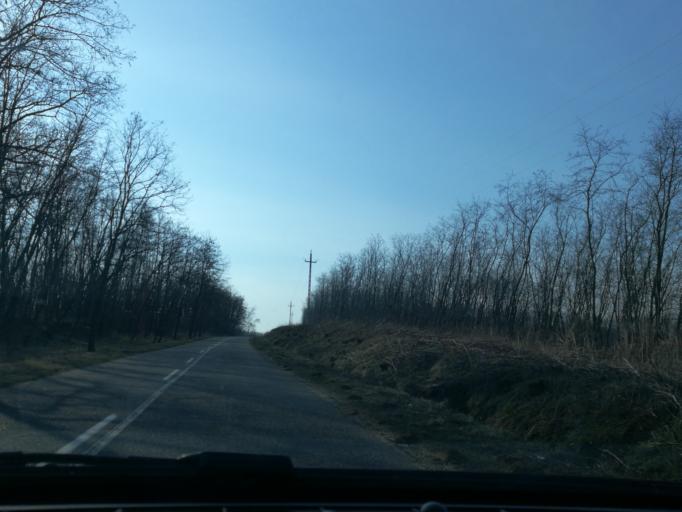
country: HU
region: Szabolcs-Szatmar-Bereg
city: Levelek
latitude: 47.9989
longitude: 21.9656
